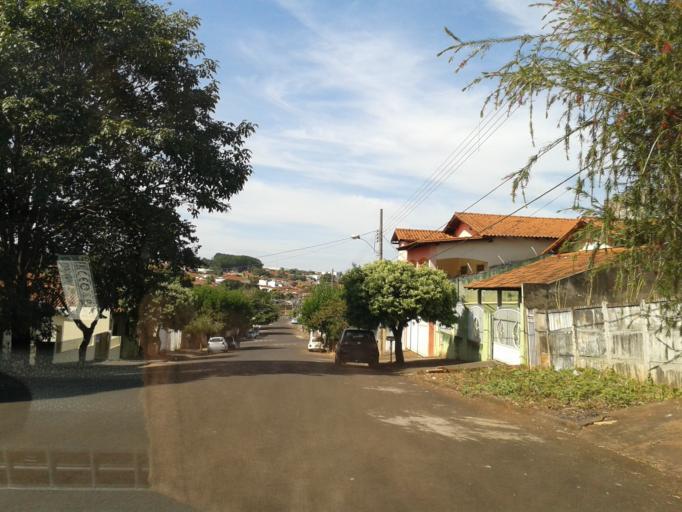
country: BR
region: Minas Gerais
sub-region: Ituiutaba
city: Ituiutaba
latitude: -18.9638
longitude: -49.4643
